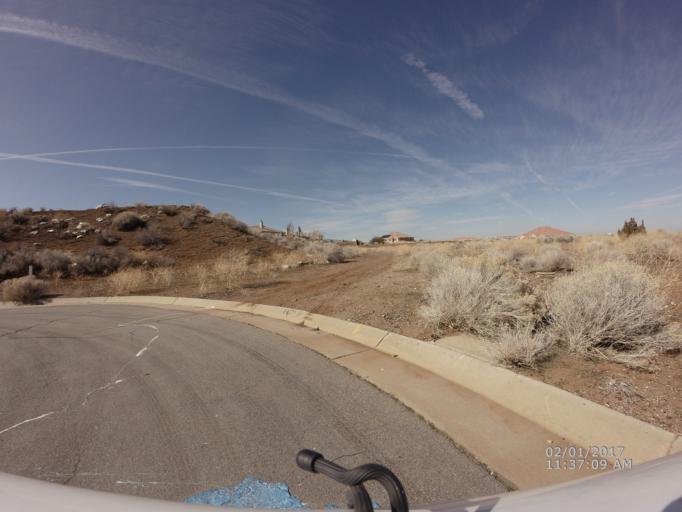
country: US
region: California
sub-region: Los Angeles County
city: Palmdale
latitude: 34.5439
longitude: -118.1187
